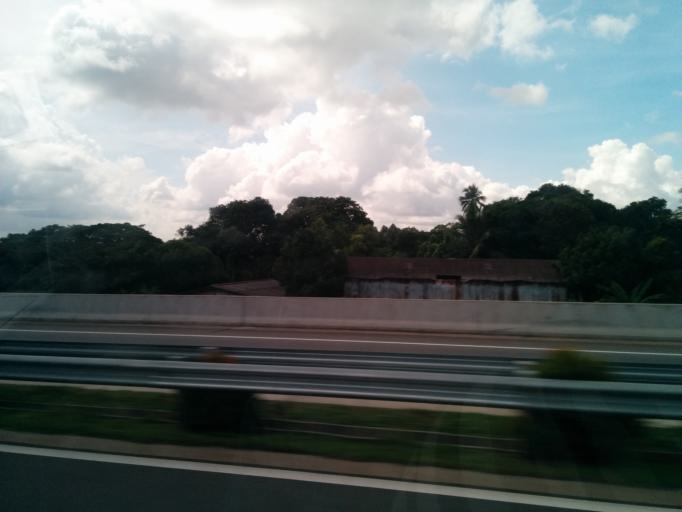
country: LK
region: Western
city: Wattala
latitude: 6.9887
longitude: 79.9006
